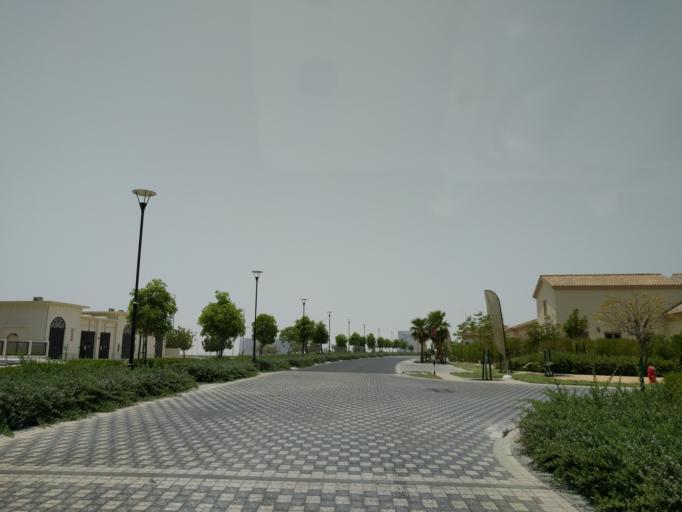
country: AE
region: Abu Dhabi
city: Abu Dhabi
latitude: 24.5498
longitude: 54.4513
